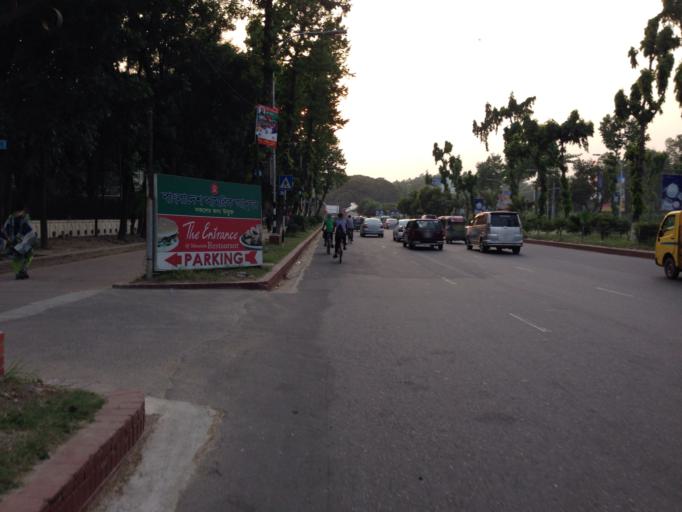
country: BD
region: Dhaka
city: Azimpur
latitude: 23.7647
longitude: 90.3856
